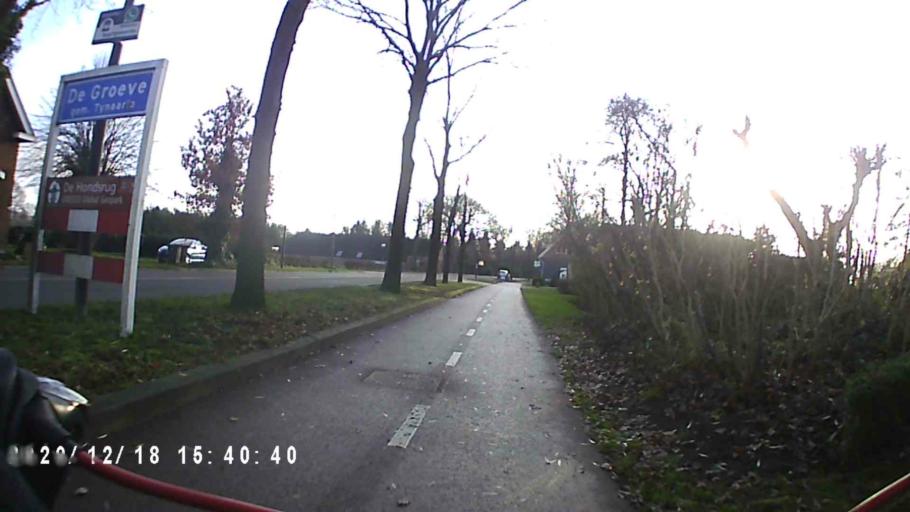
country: NL
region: Drenthe
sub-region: Gemeente Tynaarlo
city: Zuidlaren
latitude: 53.1200
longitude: 6.7211
